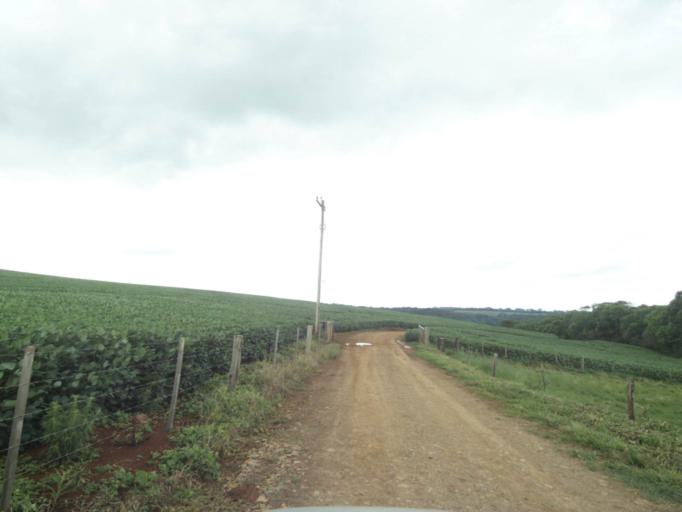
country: BR
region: Rio Grande do Sul
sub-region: Lagoa Vermelha
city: Lagoa Vermelha
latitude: -28.2077
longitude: -51.5528
